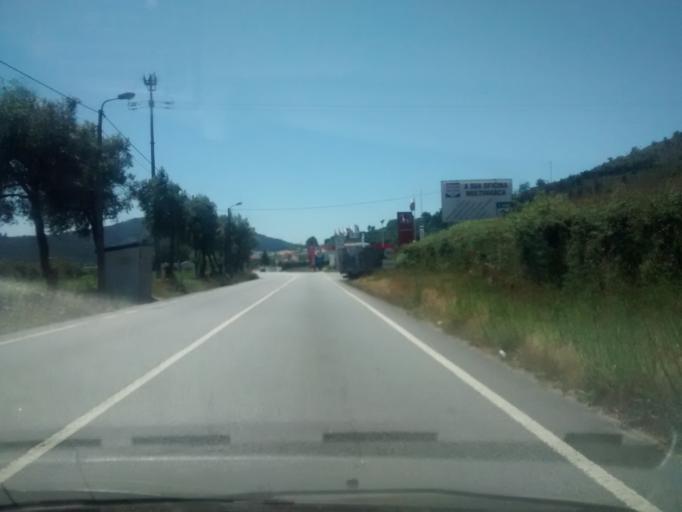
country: PT
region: Braga
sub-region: Braga
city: Braga
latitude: 41.5342
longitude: -8.4591
